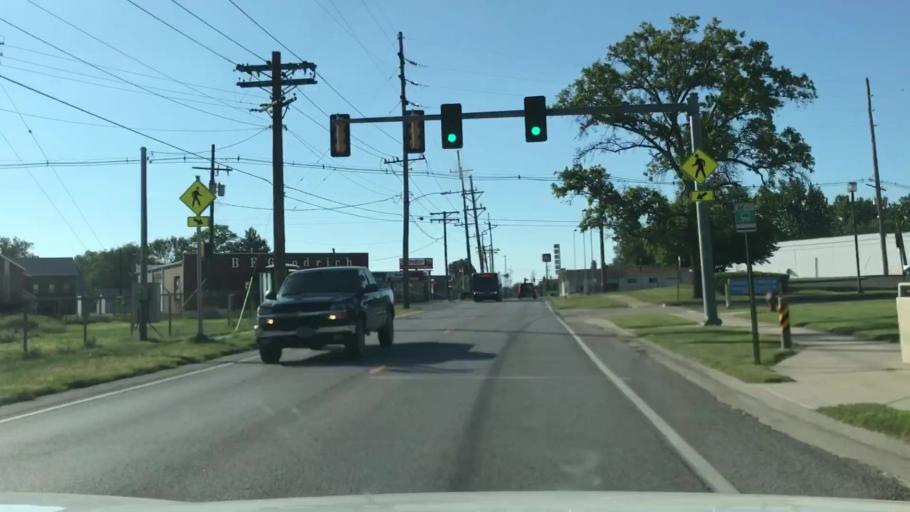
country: US
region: Illinois
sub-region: Madison County
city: Wood River
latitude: 38.8726
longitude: -90.0963
